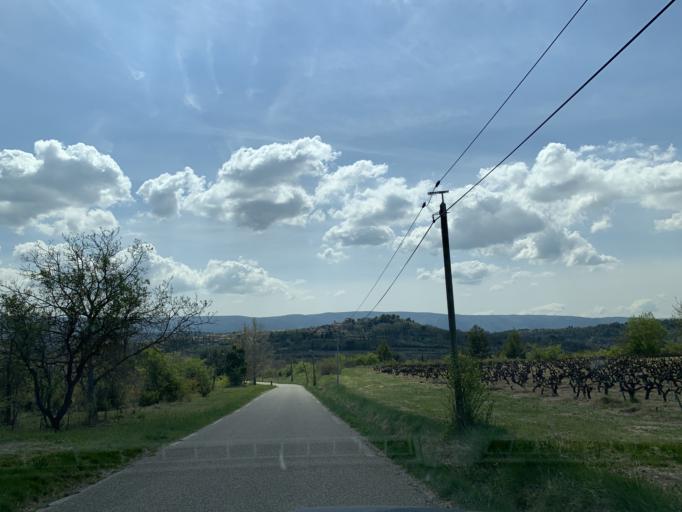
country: FR
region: Provence-Alpes-Cote d'Azur
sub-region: Departement du Vaucluse
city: Goult
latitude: 43.8732
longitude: 5.2502
